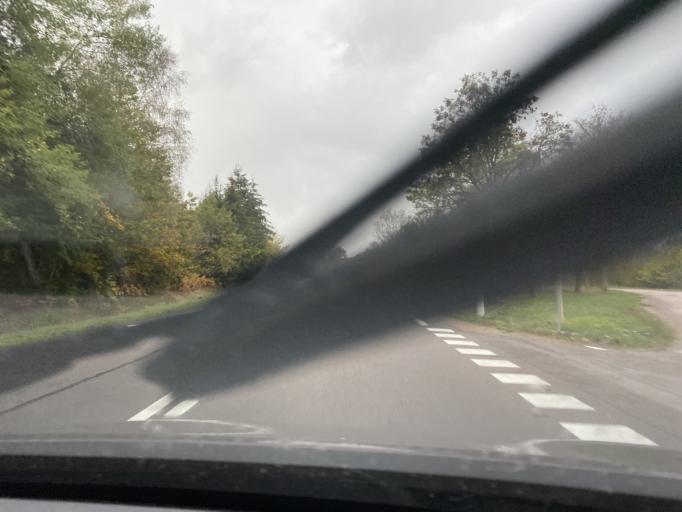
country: FR
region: Bourgogne
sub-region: Departement de la Cote-d'Or
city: Saulieu
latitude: 47.3084
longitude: 4.2074
